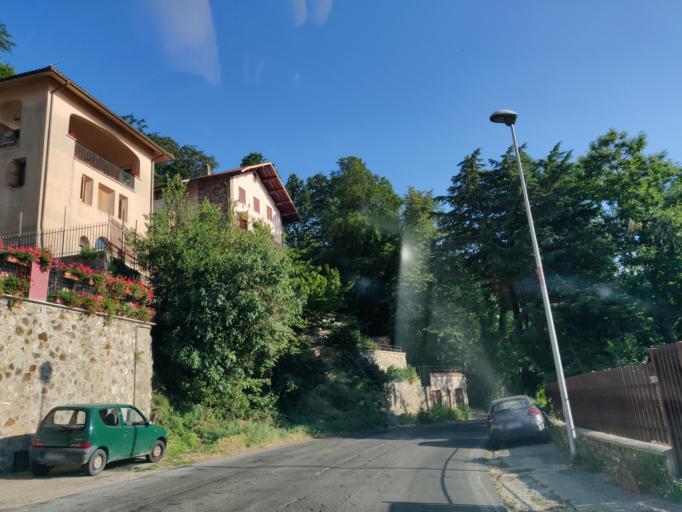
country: IT
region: Latium
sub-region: Citta metropolitana di Roma Capitale
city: Allumiere
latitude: 42.1563
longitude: 11.9073
